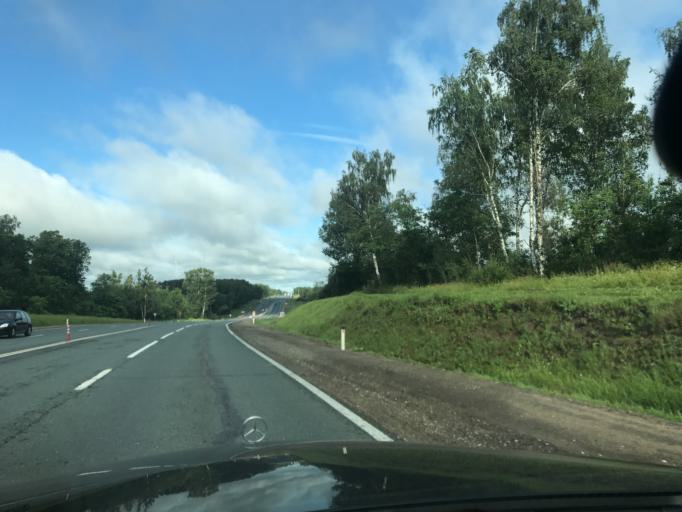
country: RU
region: Smolensk
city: Gagarin
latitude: 55.4995
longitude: 35.1926
